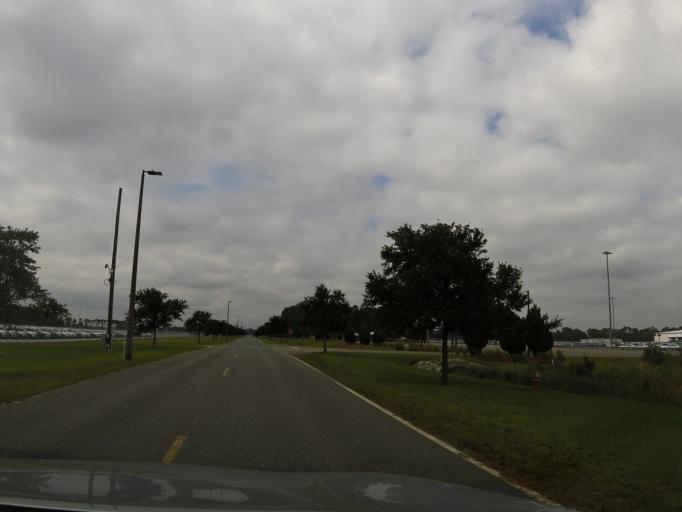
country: US
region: Georgia
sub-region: Glynn County
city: Brunswick
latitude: 31.1083
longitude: -81.5395
